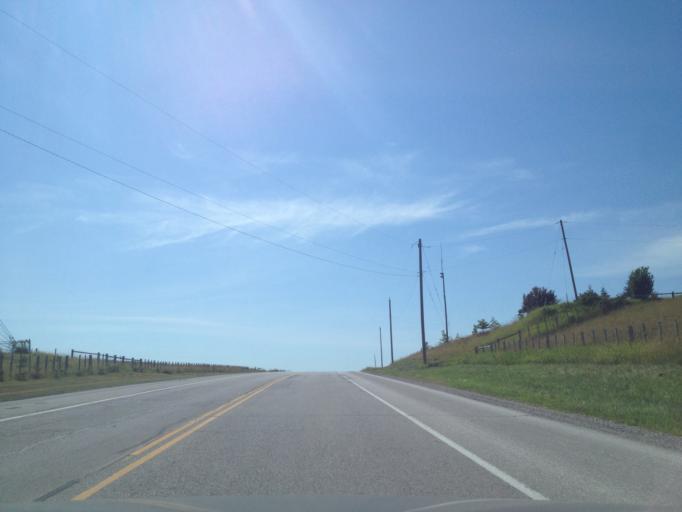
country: CA
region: Ontario
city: Waterloo
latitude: 43.5256
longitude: -80.7224
